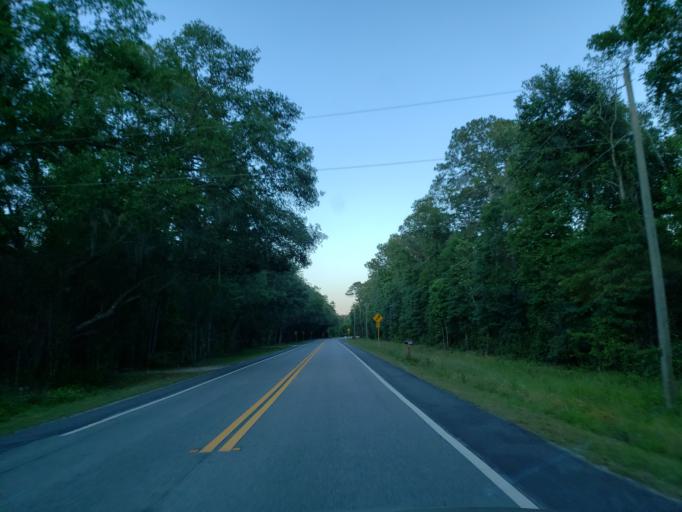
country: US
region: Georgia
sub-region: Echols County
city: Statenville
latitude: 30.5621
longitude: -83.1426
